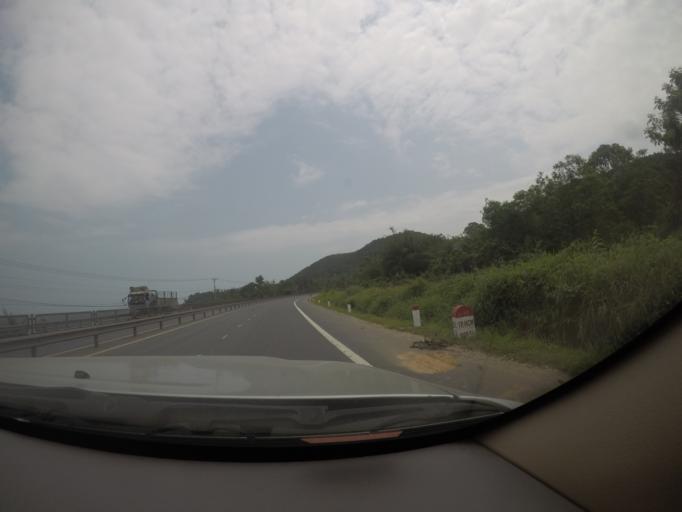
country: VN
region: Thua Thien-Hue
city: Phu Loc
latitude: 16.2878
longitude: 107.8492
